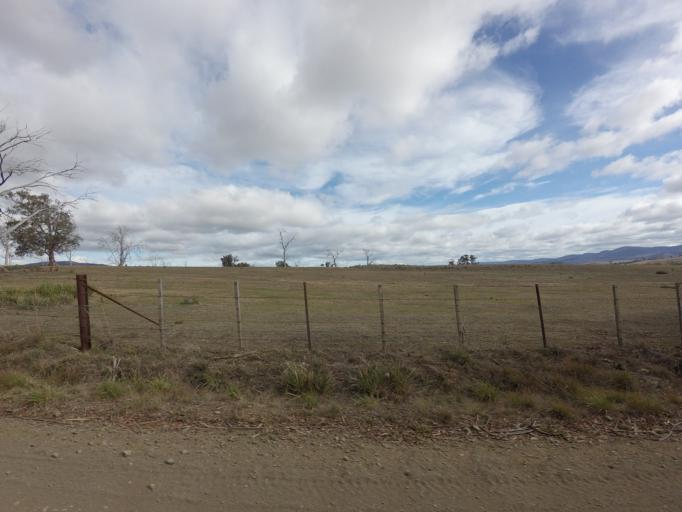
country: AU
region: Tasmania
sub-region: Brighton
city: Bridgewater
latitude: -42.4588
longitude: 147.2544
